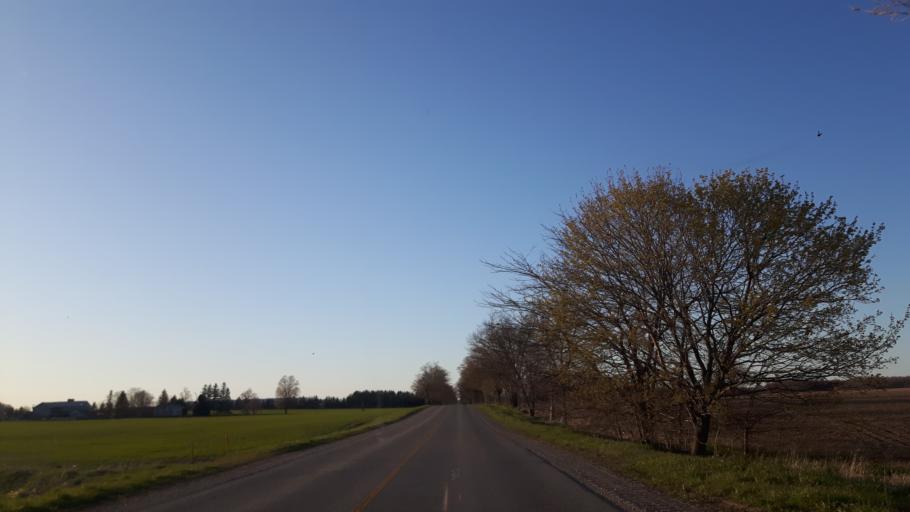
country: CA
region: Ontario
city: Bluewater
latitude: 43.5280
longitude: -81.5436
